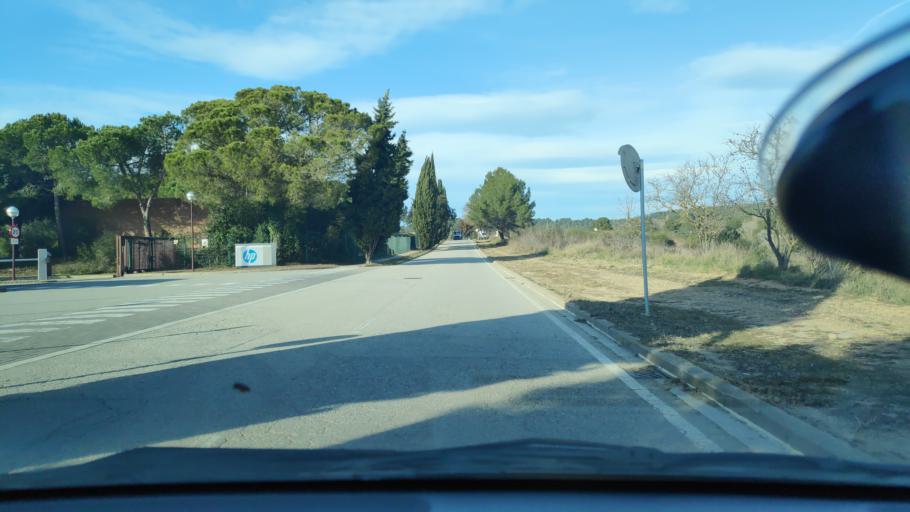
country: ES
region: Catalonia
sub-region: Provincia de Barcelona
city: Sant Cugat del Valles
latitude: 41.4922
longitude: 2.0660
